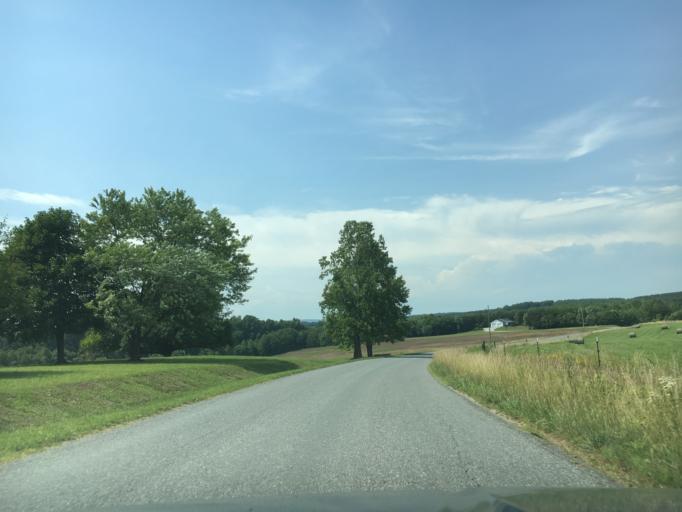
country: US
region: Virginia
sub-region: Pittsylvania County
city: Gretna
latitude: 36.9374
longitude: -79.4414
